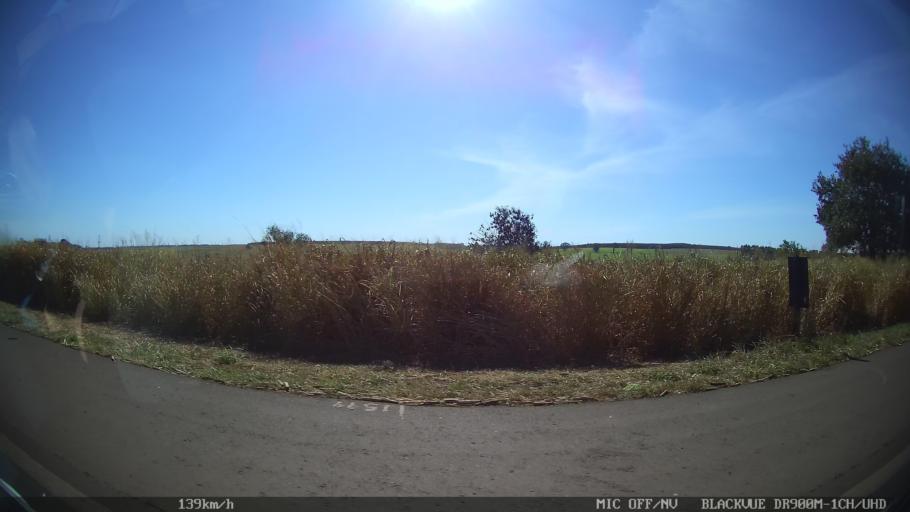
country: BR
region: Sao Paulo
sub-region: Olimpia
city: Olimpia
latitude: -20.6773
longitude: -48.8888
